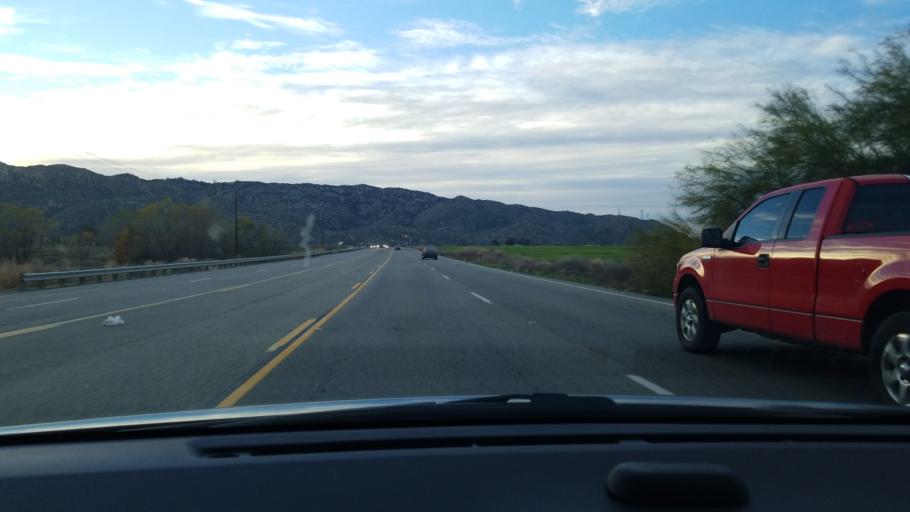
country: US
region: California
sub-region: Riverside County
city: San Jacinto
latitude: 33.8235
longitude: -117.0270
